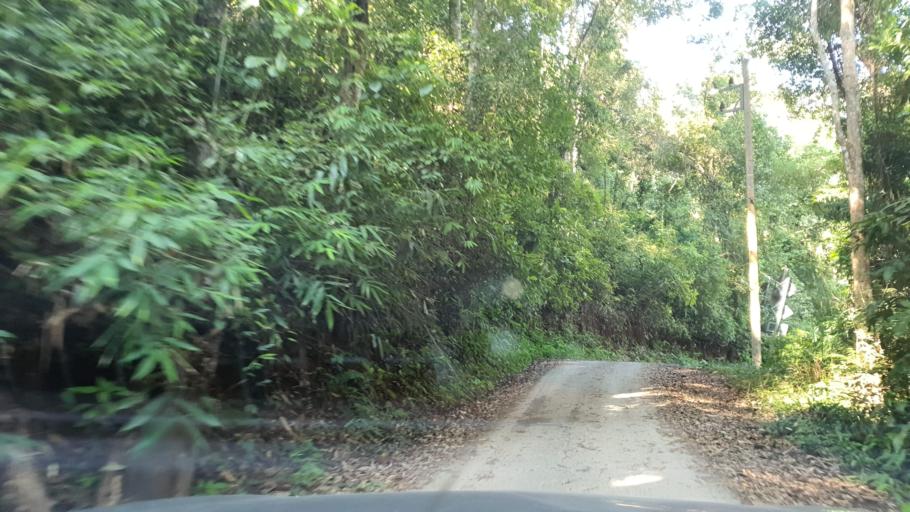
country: TH
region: Chiang Mai
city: Chiang Mai
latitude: 18.8315
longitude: 98.8954
